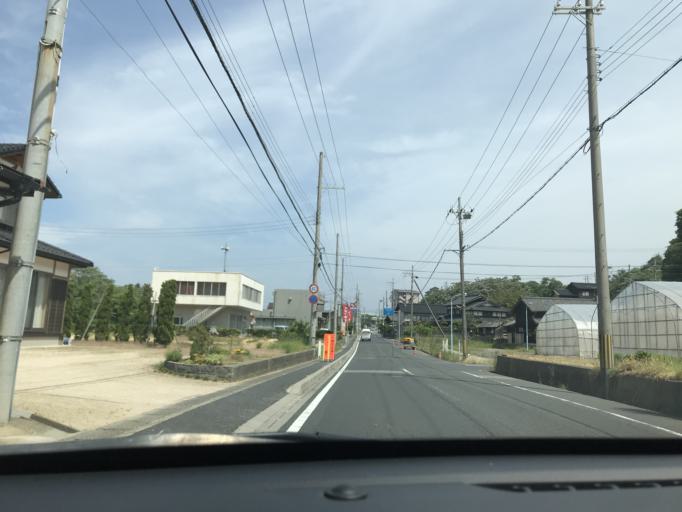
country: JP
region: Hyogo
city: Toyooka
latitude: 35.6551
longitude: 134.9690
